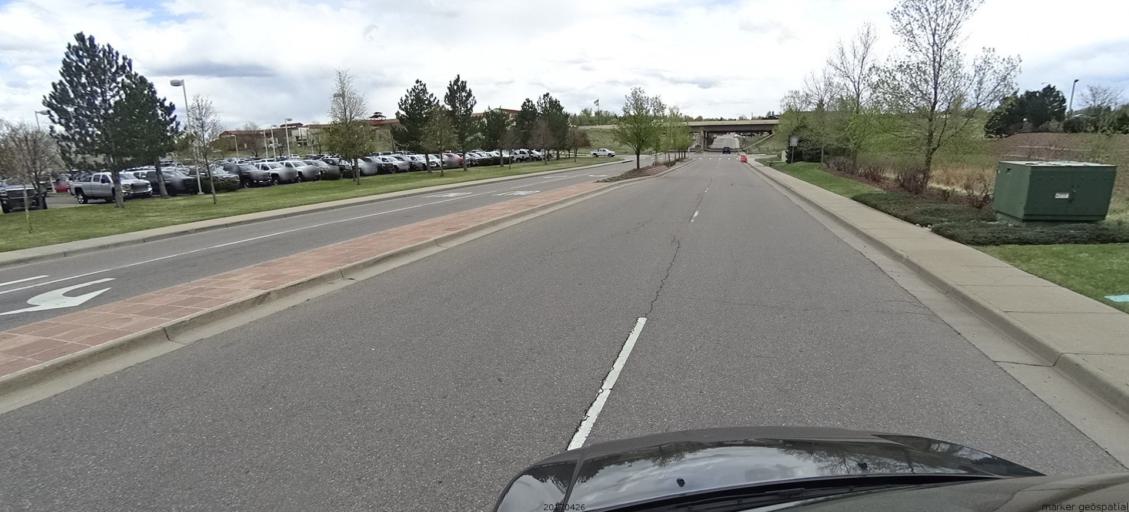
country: US
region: Colorado
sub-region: Douglas County
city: Acres Green
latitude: 39.5658
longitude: -104.8972
